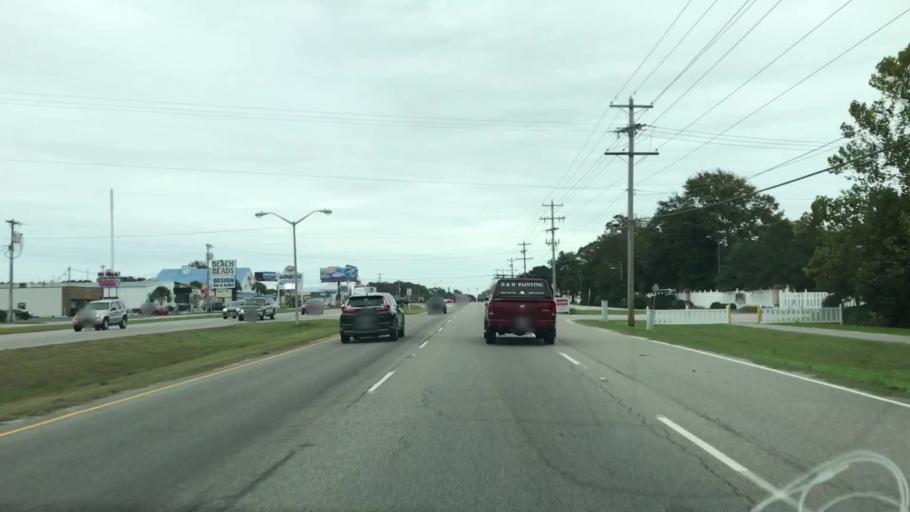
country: US
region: South Carolina
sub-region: Horry County
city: Surfside Beach
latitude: 33.6268
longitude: -78.9655
